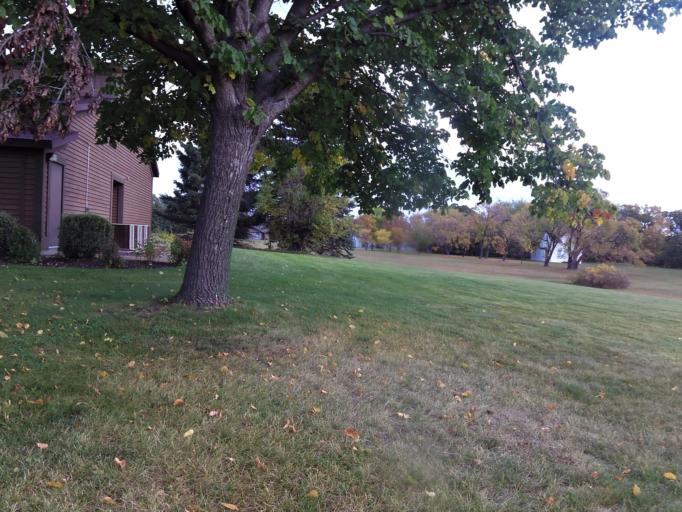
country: US
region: North Dakota
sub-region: Pembina County
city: Cavalier
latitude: 48.7736
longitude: -97.7396
